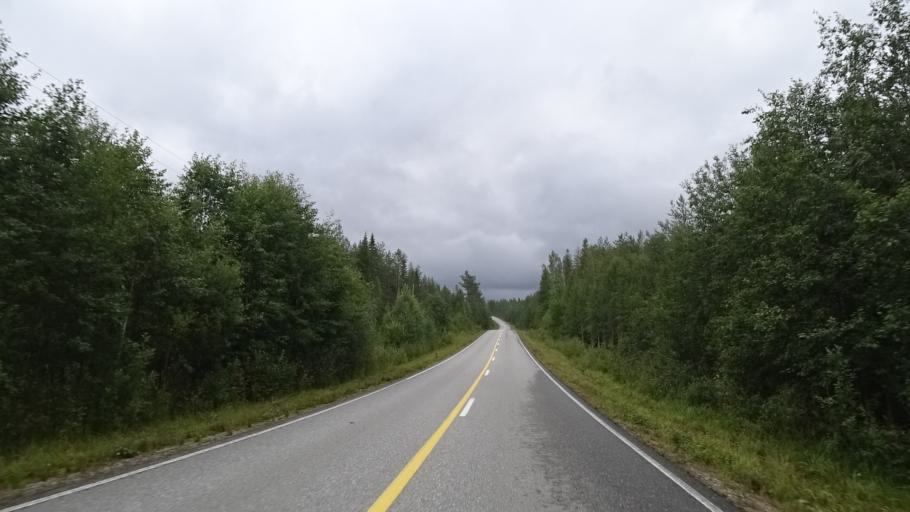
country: FI
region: North Karelia
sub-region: Joensuu
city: Ilomantsi
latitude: 63.2506
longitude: 30.7191
